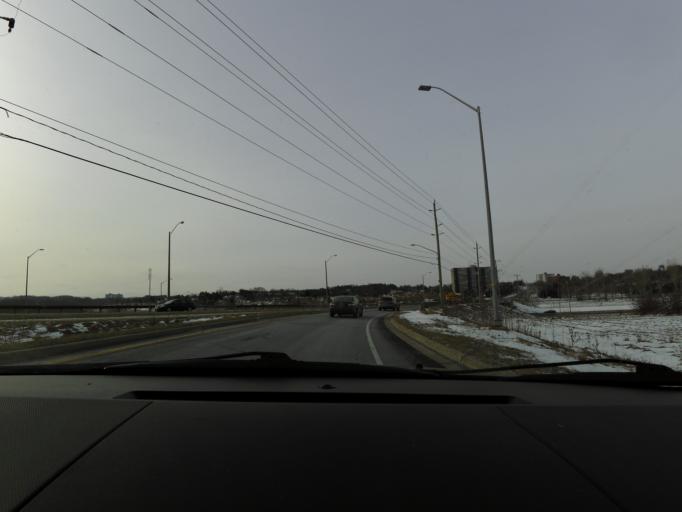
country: CA
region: Ontario
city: Waterloo
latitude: 43.4872
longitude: -80.4997
